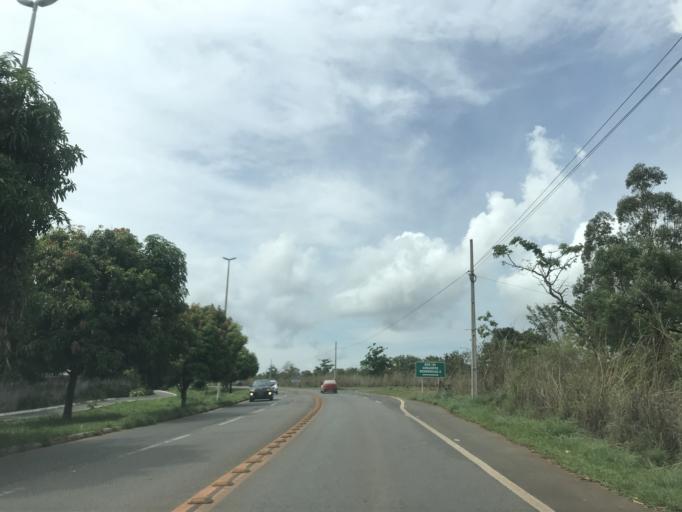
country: BR
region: Federal District
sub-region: Brasilia
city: Brasilia
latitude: -15.6845
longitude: -47.8376
